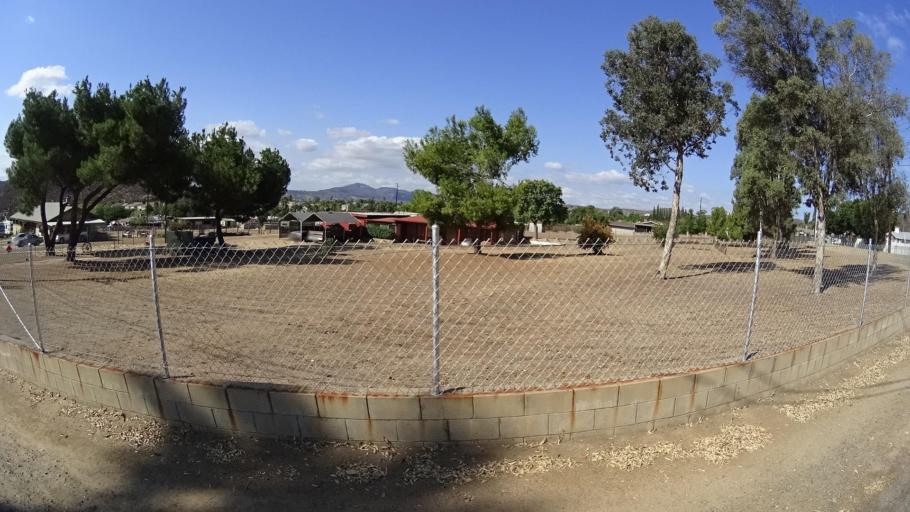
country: US
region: California
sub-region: San Diego County
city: Eucalyptus Hills
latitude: 32.8633
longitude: -116.9553
